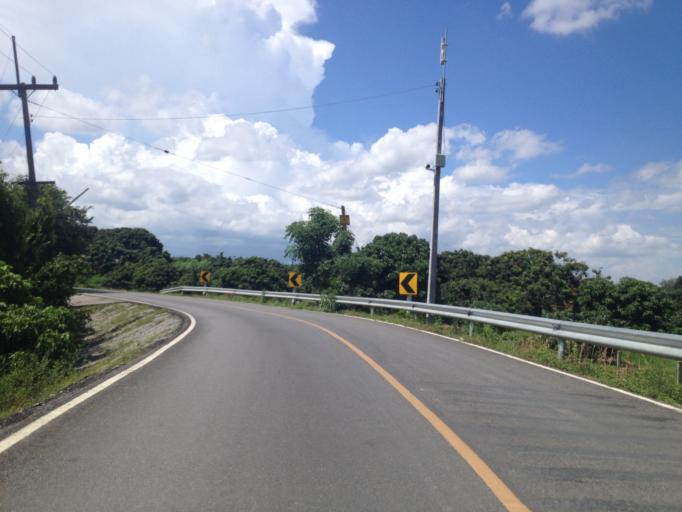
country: TH
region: Chiang Mai
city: Hang Dong
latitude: 18.6587
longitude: 98.9642
